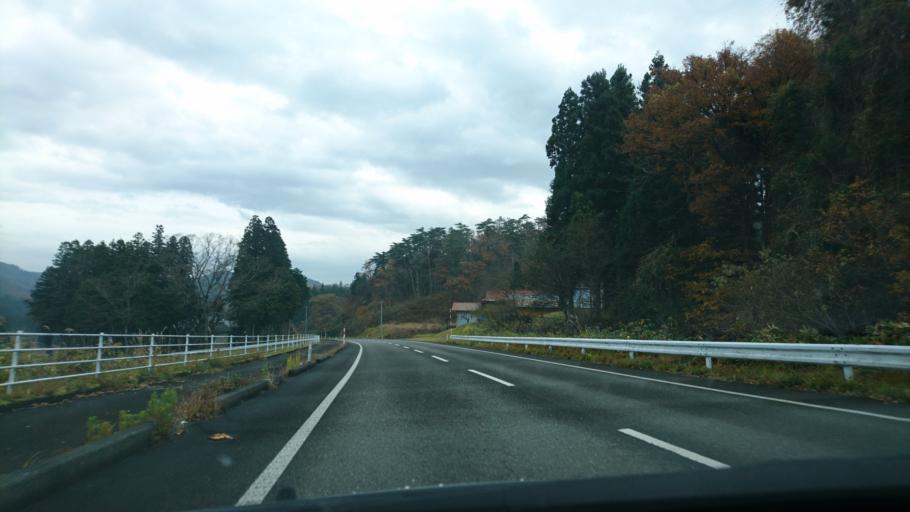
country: JP
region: Iwate
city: Ichinoseki
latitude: 38.8970
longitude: 140.9320
